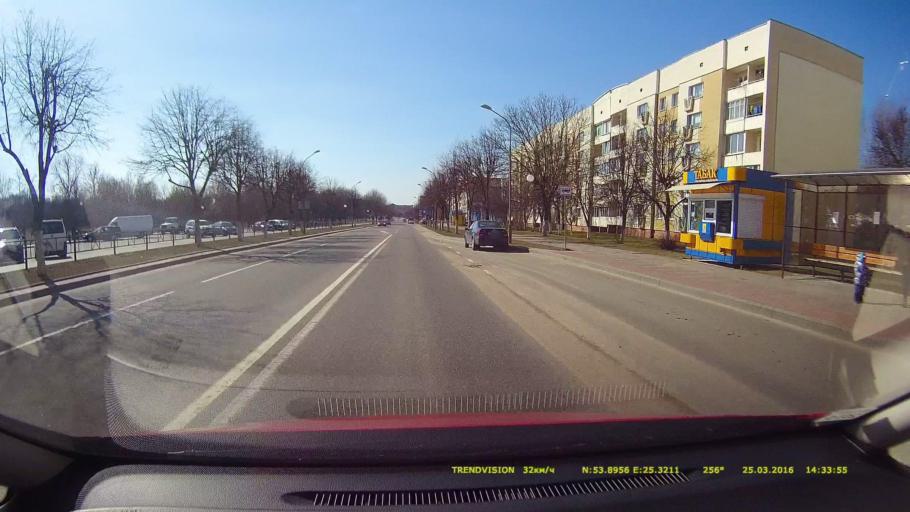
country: BY
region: Grodnenskaya
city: Lida
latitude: 53.8956
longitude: 25.3212
